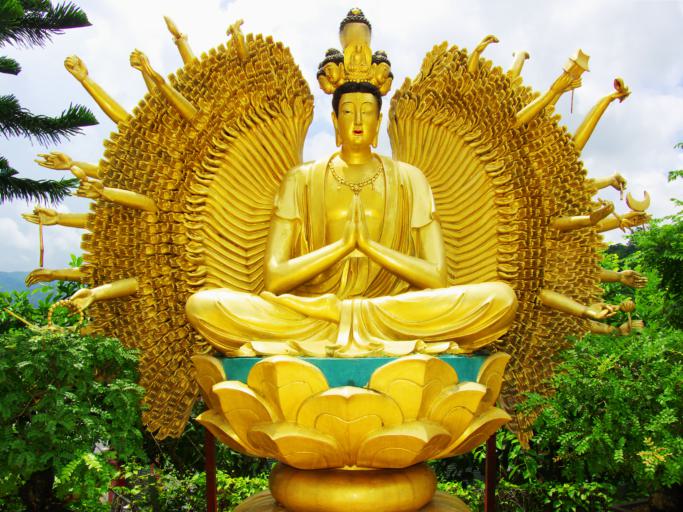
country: HK
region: Sha Tin
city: Sha Tin
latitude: 22.3871
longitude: 114.1849
